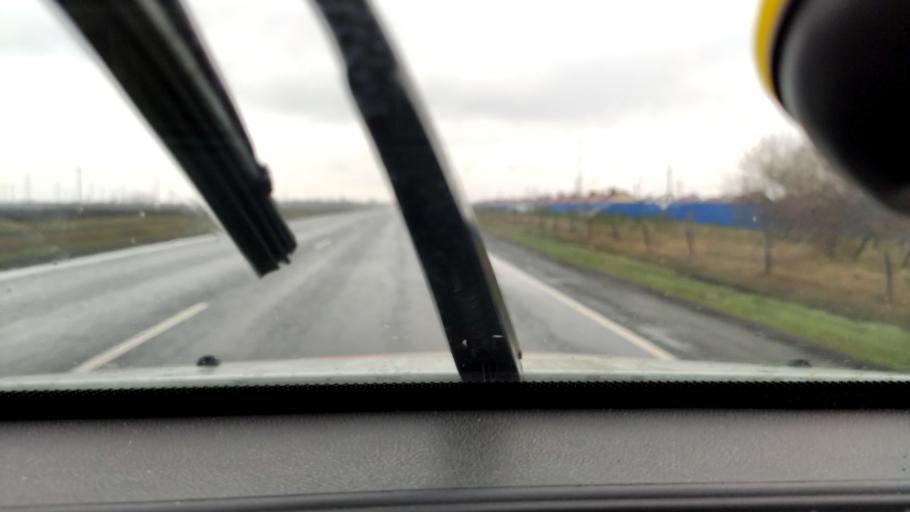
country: RU
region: Samara
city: Povolzhskiy
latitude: 53.6443
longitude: 49.6687
